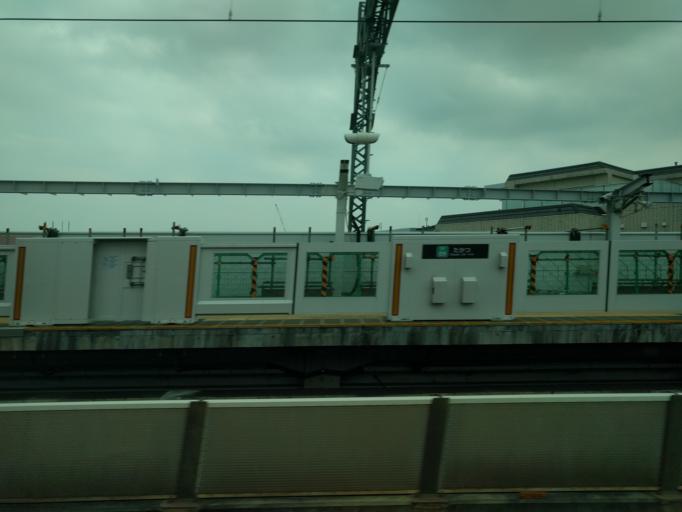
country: JP
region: Tokyo
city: Chofugaoka
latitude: 35.6042
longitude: 139.6190
